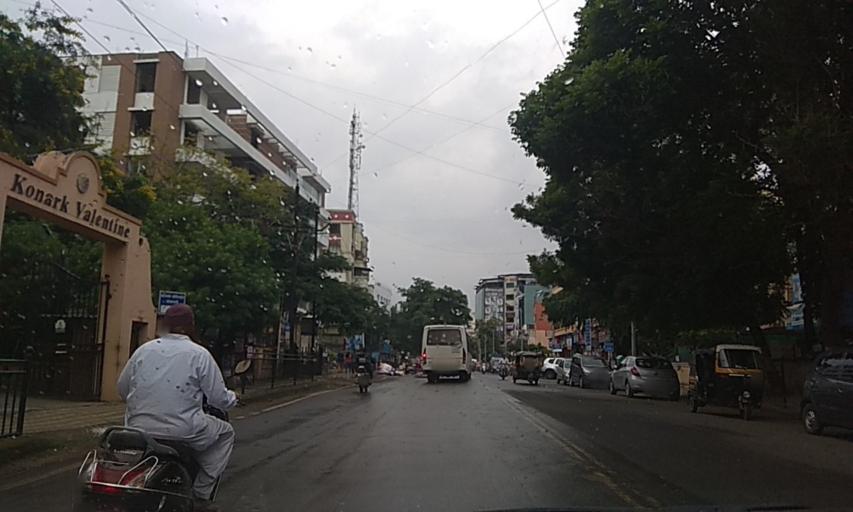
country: IN
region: Maharashtra
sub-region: Pune Division
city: Lohogaon
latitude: 18.5652
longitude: 73.9158
